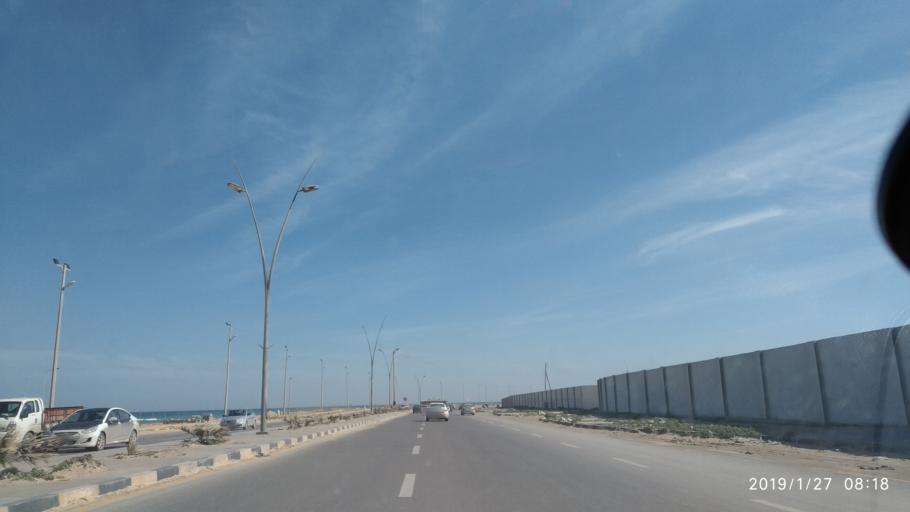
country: LY
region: Tripoli
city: Tagiura
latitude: 32.9085
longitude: 13.2848
